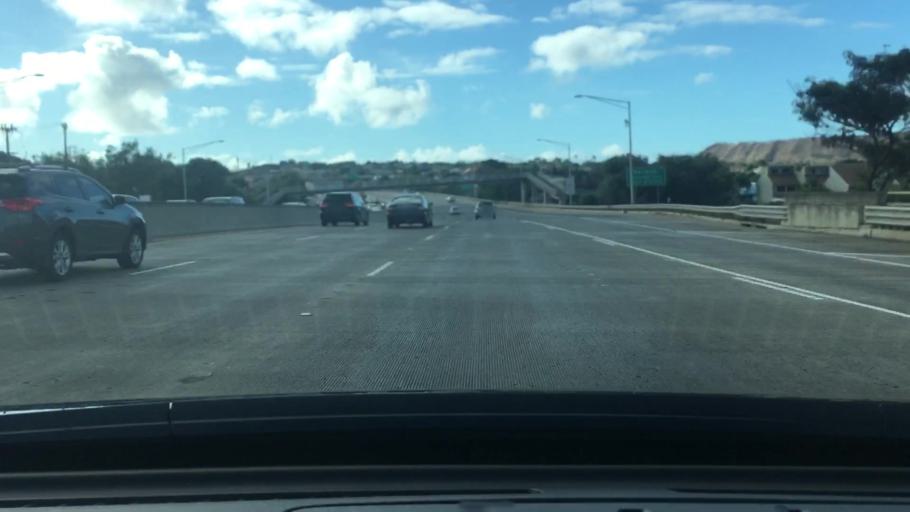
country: US
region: Hawaii
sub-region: Honolulu County
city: Honolulu
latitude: 21.2874
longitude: -157.8127
